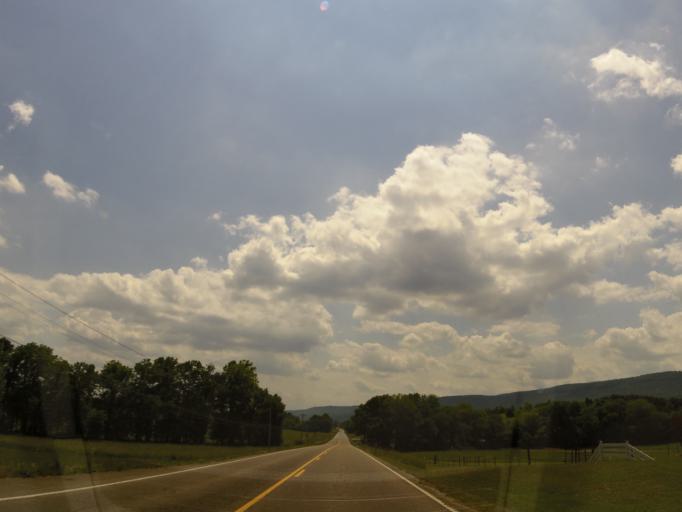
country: US
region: Tennessee
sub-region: Bledsoe County
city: Pikeville
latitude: 35.5812
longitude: -85.2200
